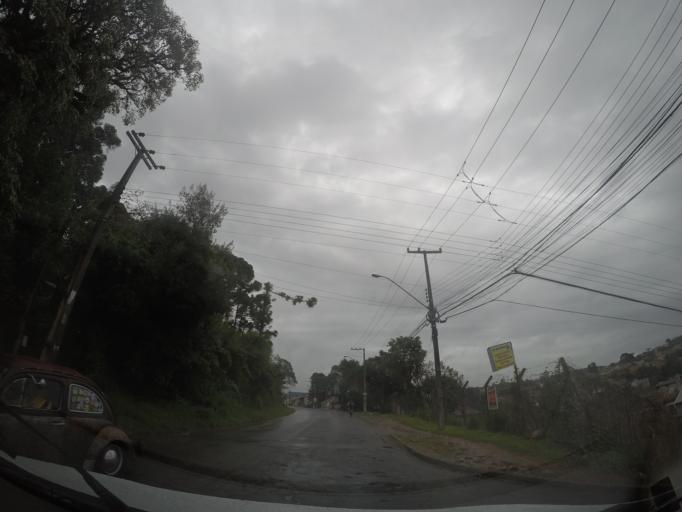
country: BR
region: Parana
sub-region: Curitiba
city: Curitiba
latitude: -25.4591
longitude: -49.3890
